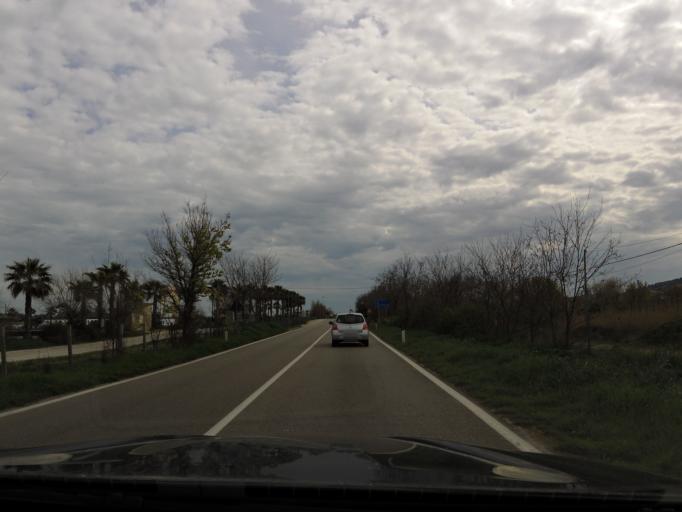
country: IT
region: The Marches
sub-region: Provincia di Macerata
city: Porto Potenza Picena
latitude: 43.3929
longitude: 13.6809
